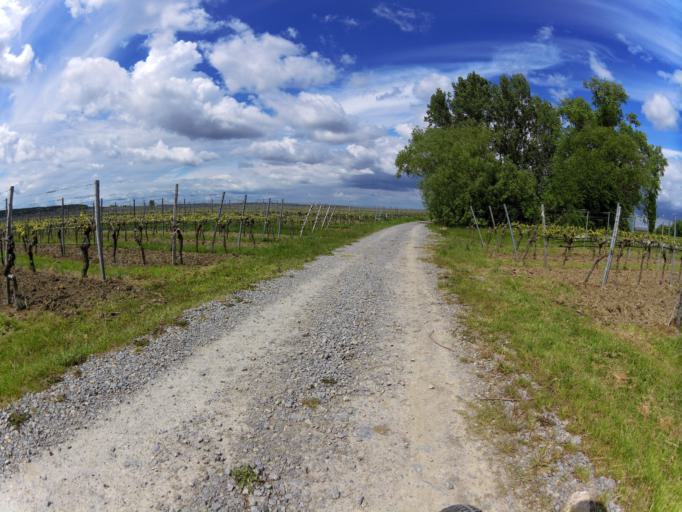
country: DE
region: Bavaria
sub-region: Regierungsbezirk Unterfranken
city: Nordheim
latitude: 49.8452
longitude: 10.1910
